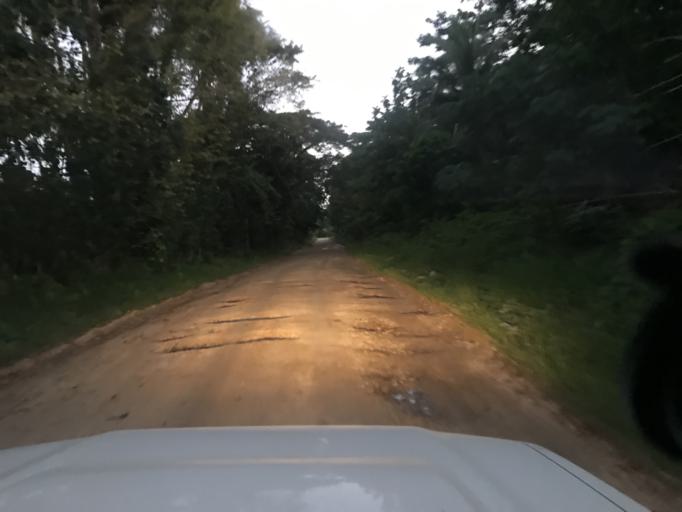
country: VU
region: Sanma
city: Luganville
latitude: -15.5712
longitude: 166.9975
